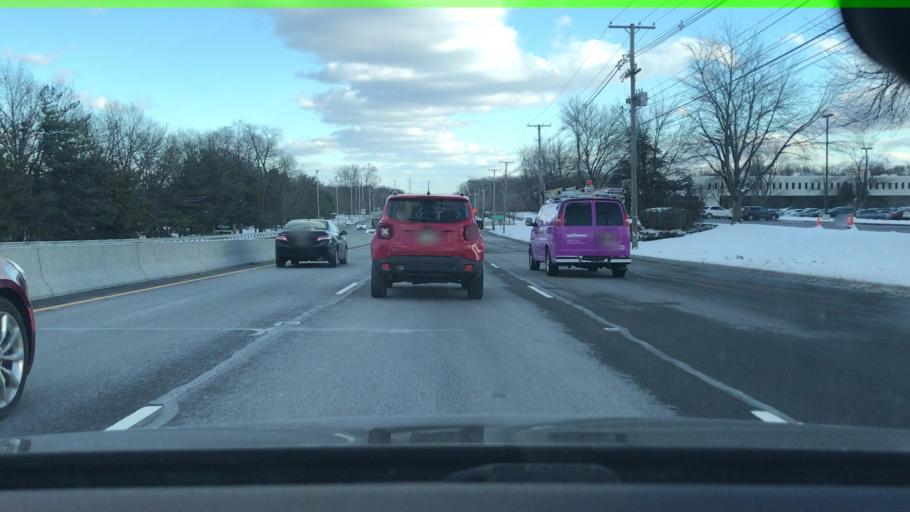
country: US
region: New Jersey
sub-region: Morris County
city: Morris Plains
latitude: 40.8408
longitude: -74.4573
